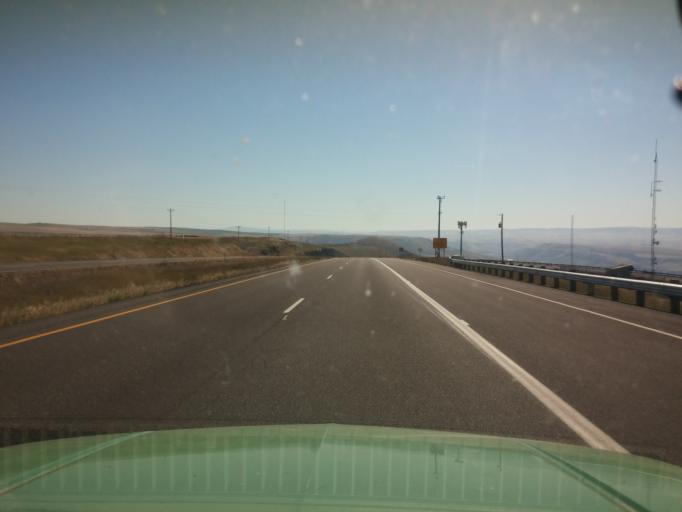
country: US
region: Idaho
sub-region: Nez Perce County
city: Lewiston
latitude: 46.4619
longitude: -117.0116
